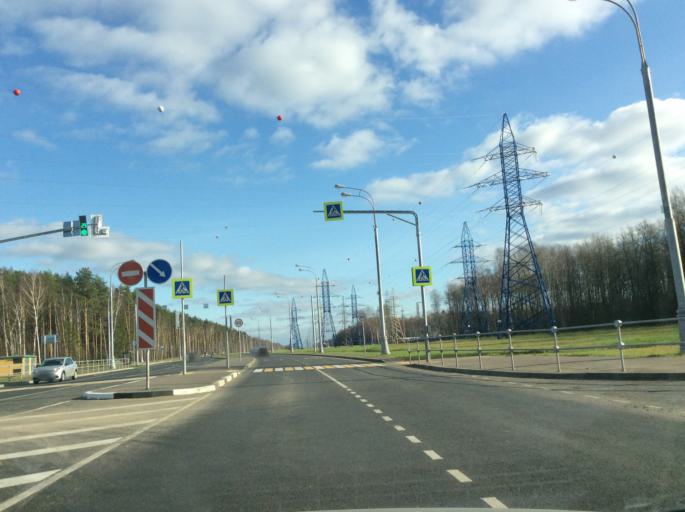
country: RU
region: Moskovskaya
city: Vatutinki
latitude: 55.4840
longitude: 37.3353
